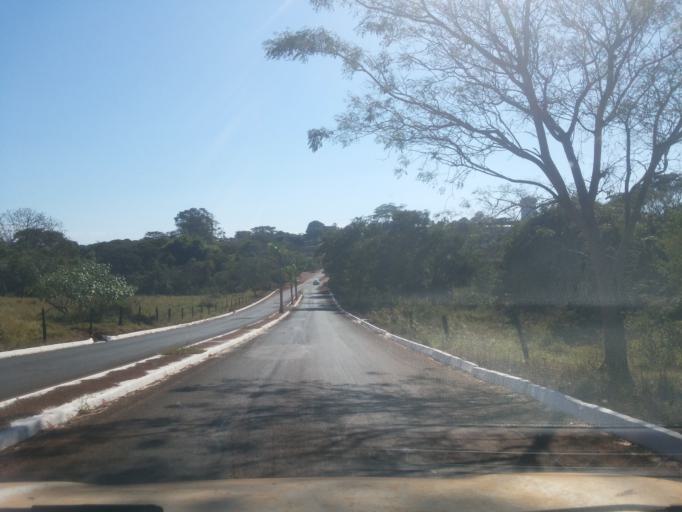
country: BR
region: Minas Gerais
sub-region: Centralina
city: Centralina
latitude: -18.7335
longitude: -49.2050
